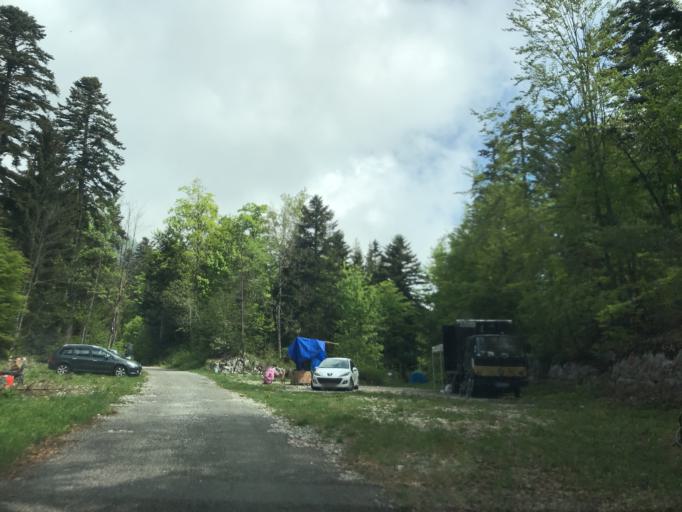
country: FR
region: Rhone-Alpes
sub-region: Departement de la Savoie
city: La Motte-Servolex
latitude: 45.5995
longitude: 5.8227
